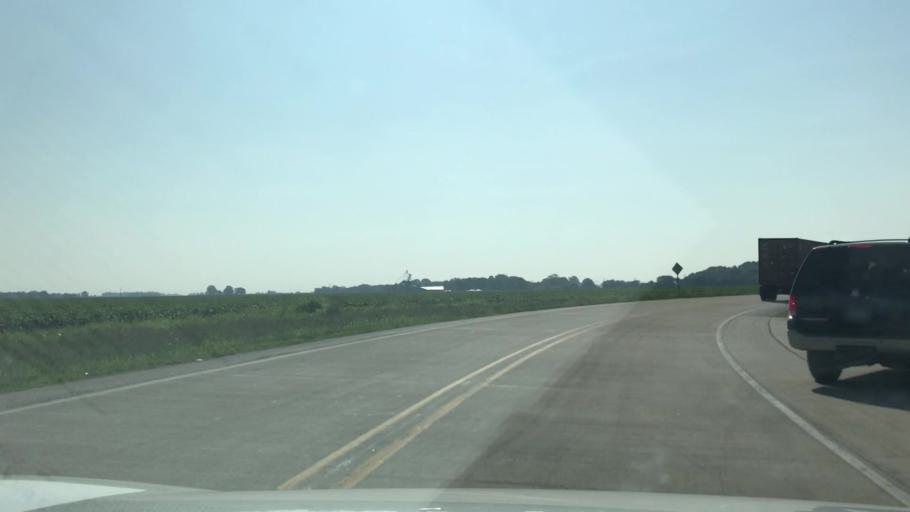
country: US
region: Illinois
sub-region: Saint Clair County
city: Scott Air Force Base
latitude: 38.5561
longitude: -89.8062
